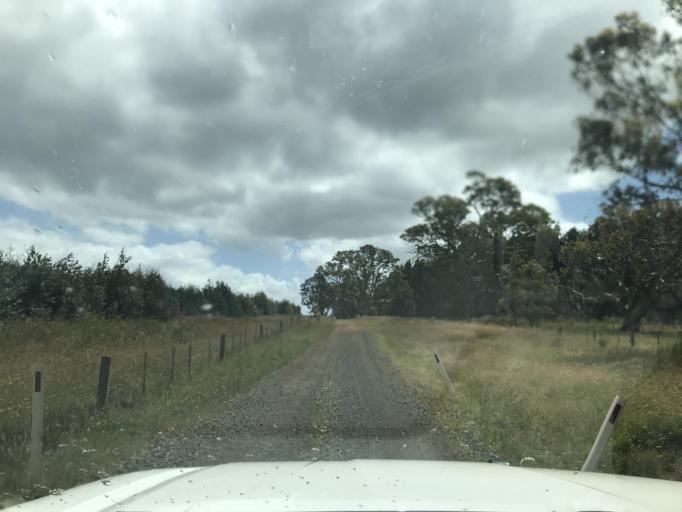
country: AU
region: South Australia
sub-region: Wattle Range
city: Penola
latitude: -37.2979
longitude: 141.4727
